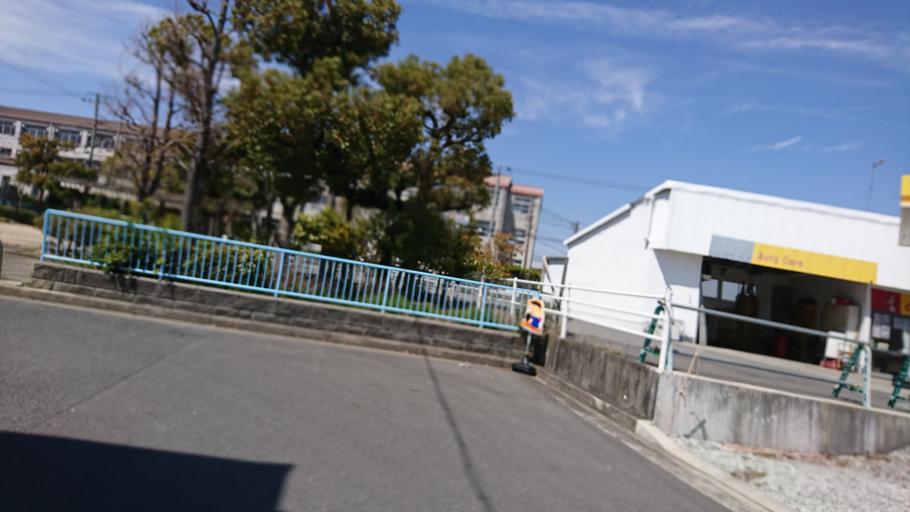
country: JP
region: Hyogo
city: Kakogawacho-honmachi
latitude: 34.7523
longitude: 134.8761
